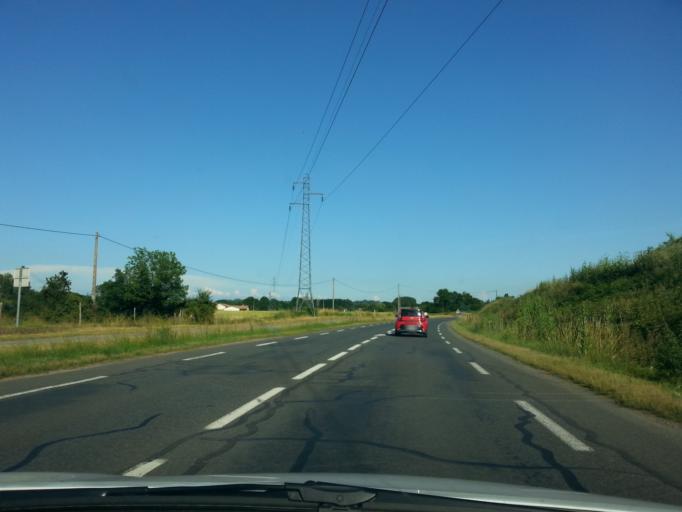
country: FR
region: Rhone-Alpes
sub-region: Departement du Rhone
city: Belleville
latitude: 46.1194
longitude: 4.7428
